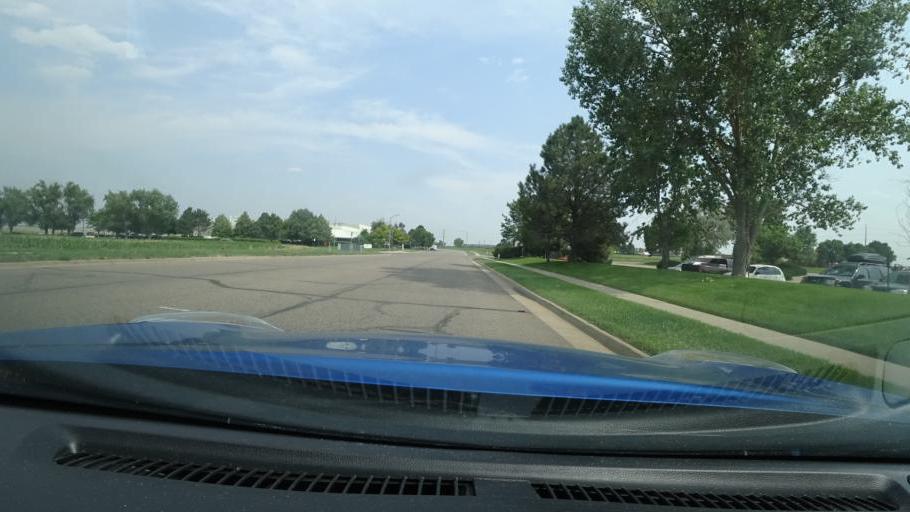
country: US
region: Colorado
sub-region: Adams County
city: Aurora
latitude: 39.7583
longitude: -104.7429
